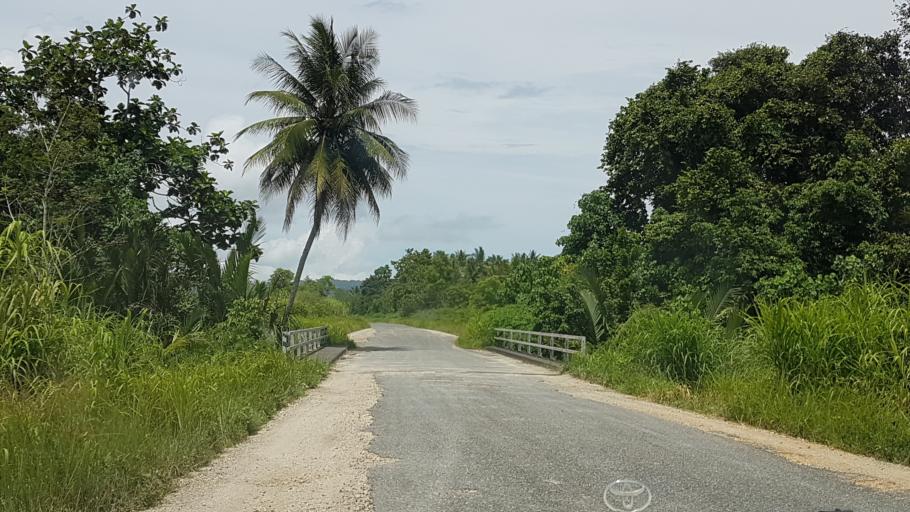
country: PG
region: Madang
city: Madang
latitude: -4.5428
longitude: 145.4939
